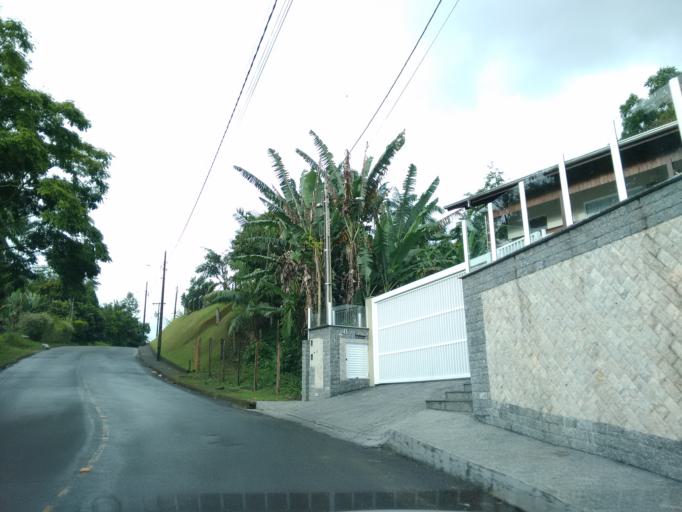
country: BR
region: Santa Catarina
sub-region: Pomerode
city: Pomerode
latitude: -26.7309
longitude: -49.1701
